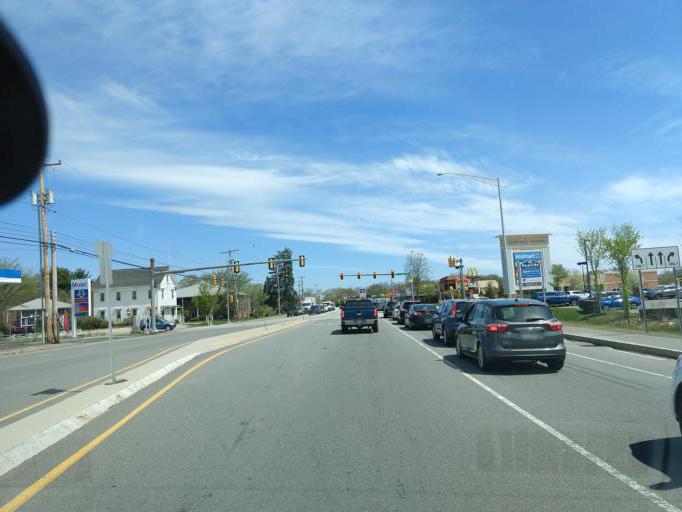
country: US
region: New Hampshire
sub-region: Rockingham County
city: Seabrook
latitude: 42.8942
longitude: -70.8720
